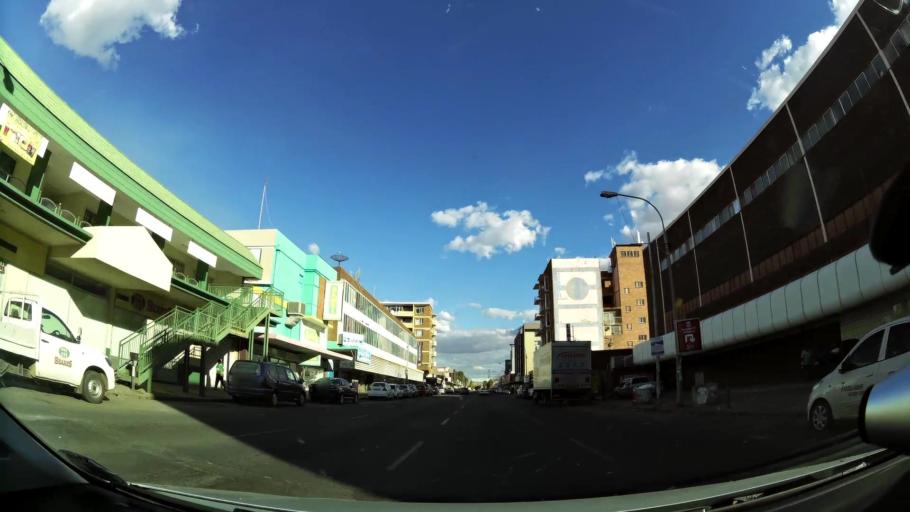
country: ZA
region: North-West
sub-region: Dr Kenneth Kaunda District Municipality
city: Klerksdorp
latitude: -26.8701
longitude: 26.6658
